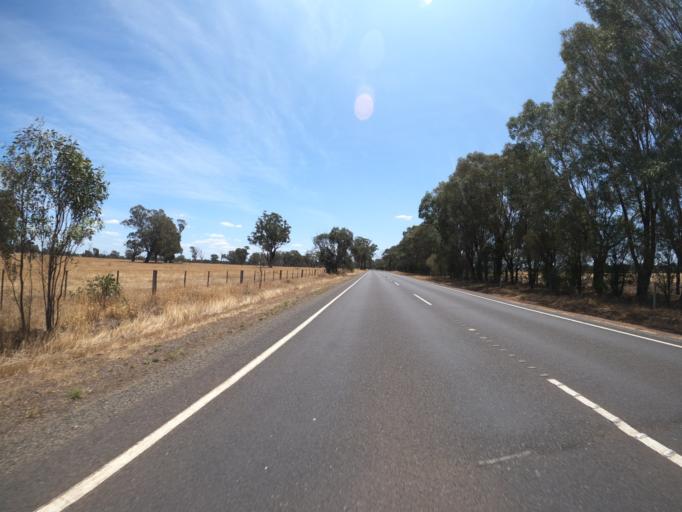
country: AU
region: Victoria
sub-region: Benalla
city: Benalla
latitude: -36.5090
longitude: 146.0274
